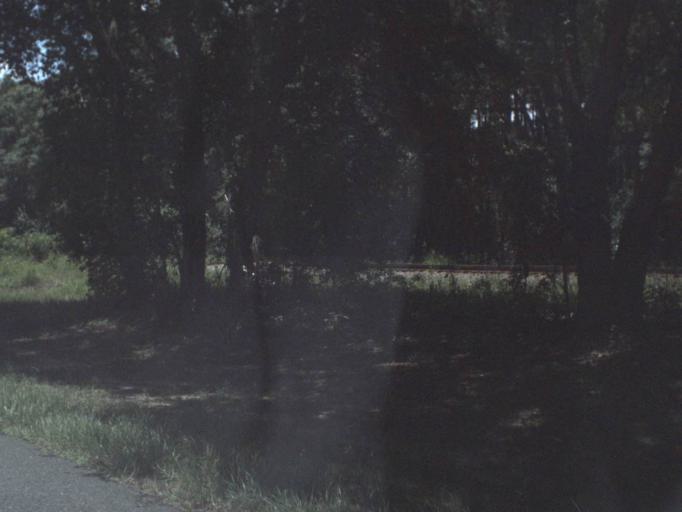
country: US
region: Florida
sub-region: Alachua County
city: Newberry
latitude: 29.5973
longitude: -82.5703
